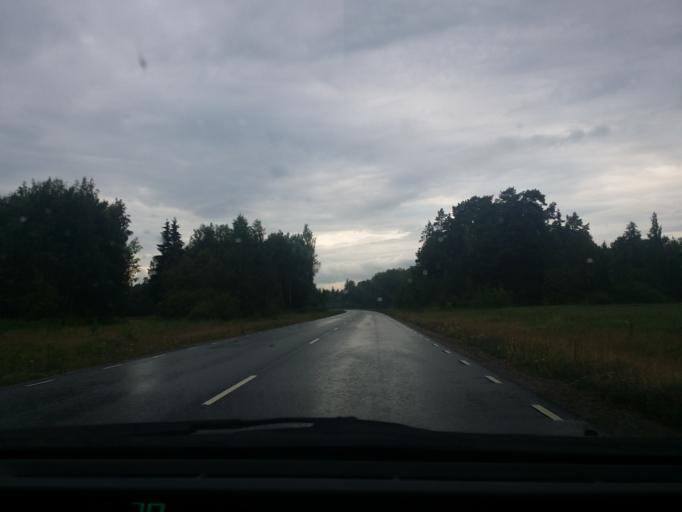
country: SE
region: Vaestmanland
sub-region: Arboga Kommun
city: Arboga
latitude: 59.4136
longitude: 15.8343
